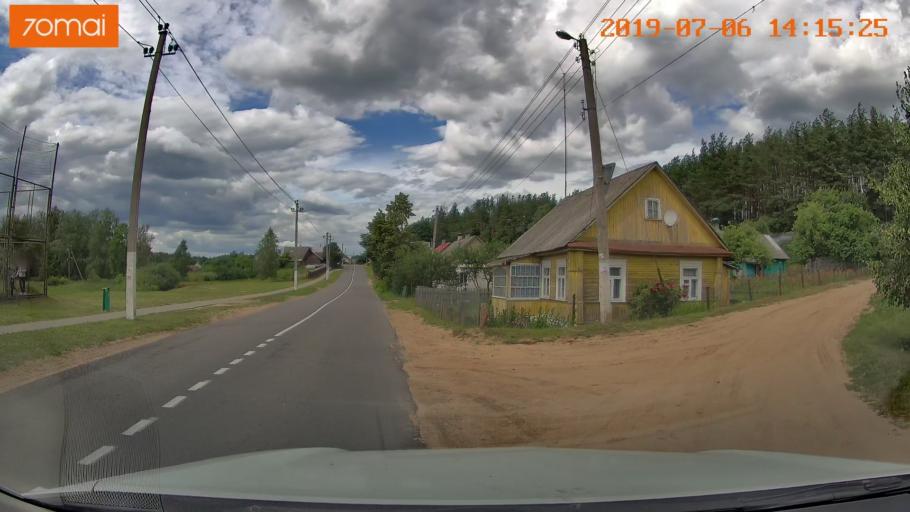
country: BY
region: Minsk
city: Ivyanyets
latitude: 53.8929
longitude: 26.7368
